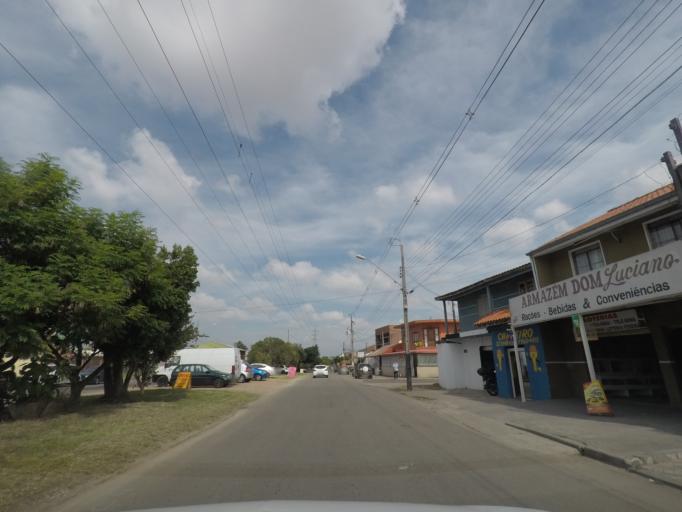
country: BR
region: Parana
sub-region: Pinhais
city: Pinhais
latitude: -25.4614
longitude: -49.1966
